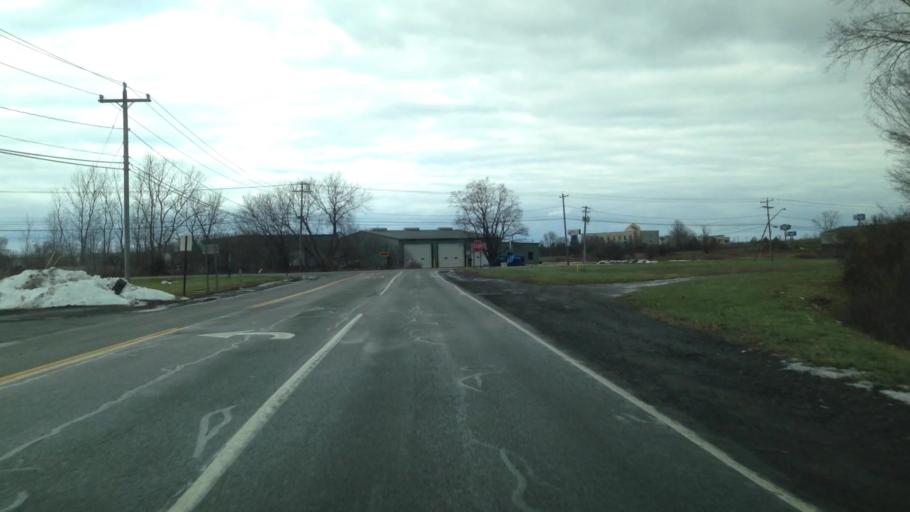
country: US
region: New York
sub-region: Genesee County
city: Batavia
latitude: 43.0160
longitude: -78.1989
